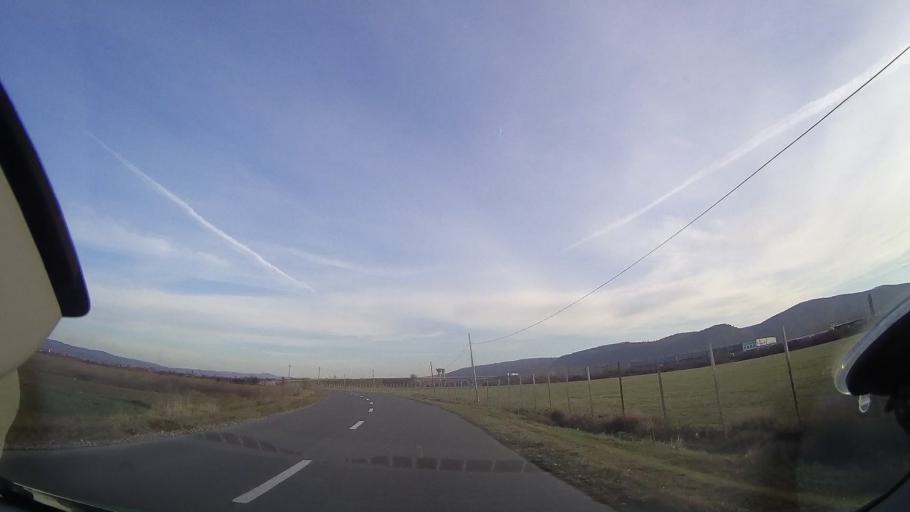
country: RO
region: Bihor
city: Lugasu de Jos
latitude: 47.0431
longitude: 22.3406
